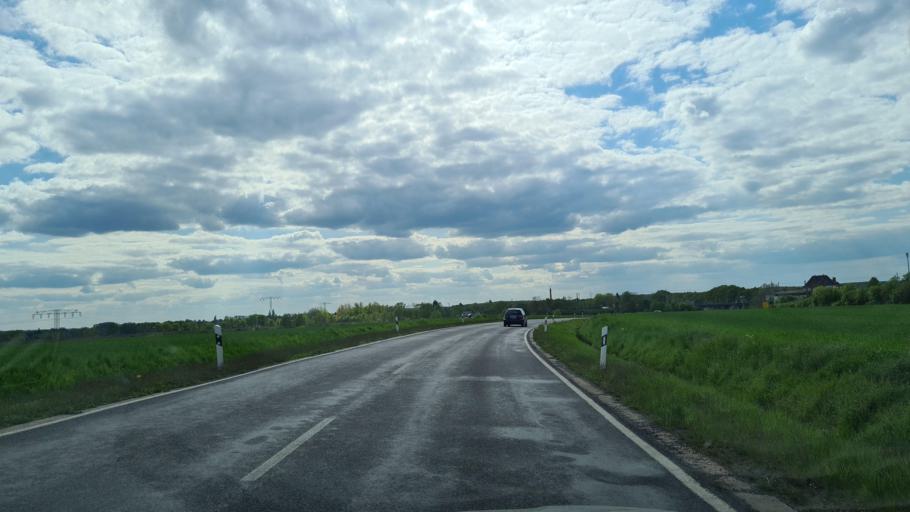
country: DE
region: Brandenburg
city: Doberlug-Kirchhain
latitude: 51.6204
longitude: 13.5716
